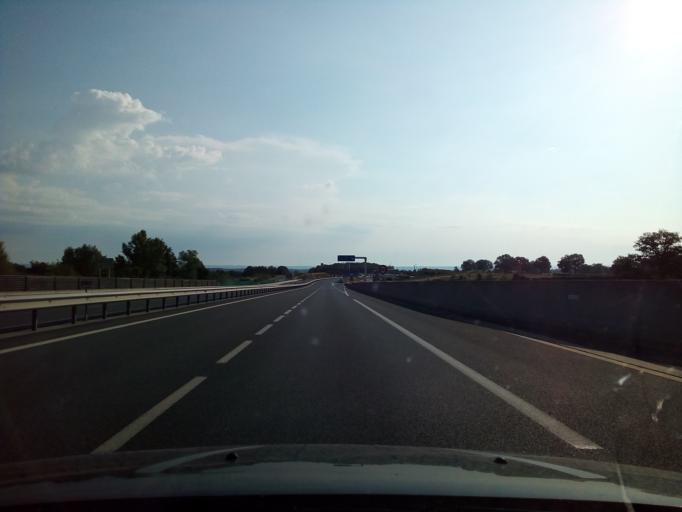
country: FR
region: Auvergne
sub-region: Departement de l'Allier
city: Desertines
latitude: 46.3923
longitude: 2.7037
